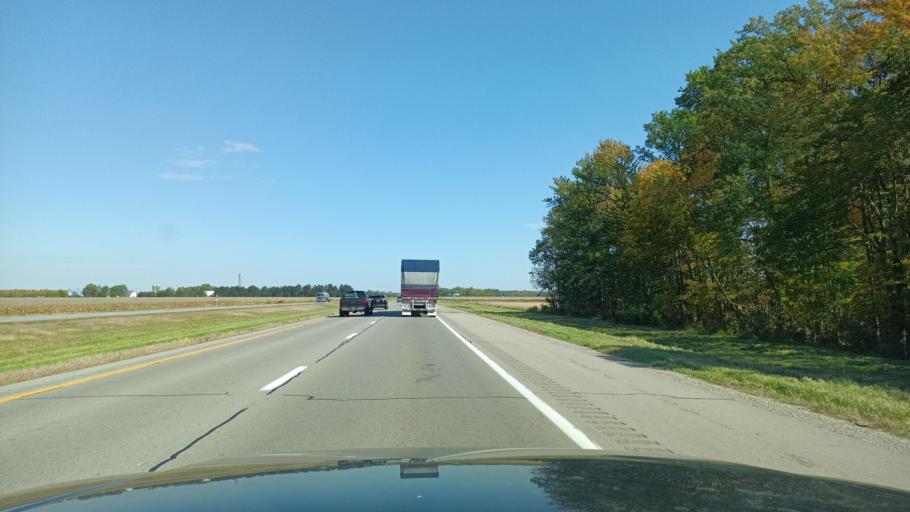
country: US
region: Ohio
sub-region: Henry County
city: Napoleon
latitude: 41.3629
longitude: -84.2128
